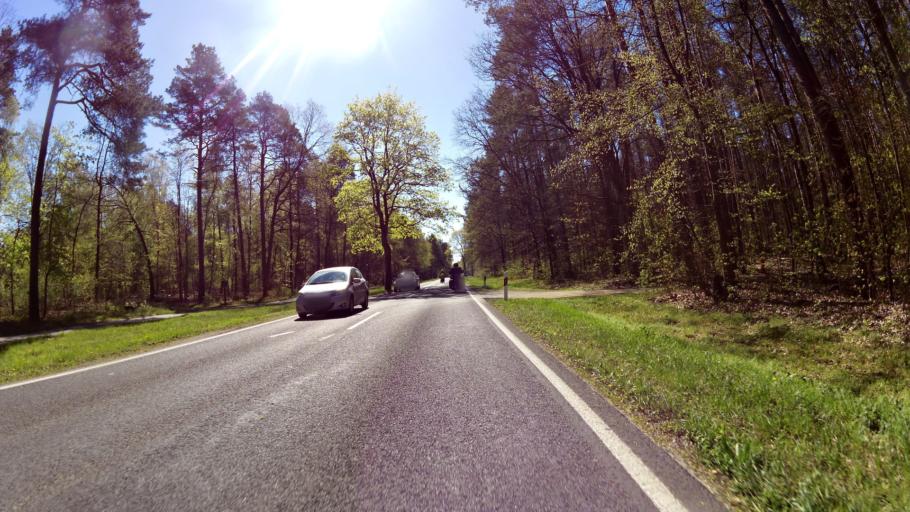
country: DE
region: Brandenburg
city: Bernau bei Berlin
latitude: 52.7117
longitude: 13.5336
